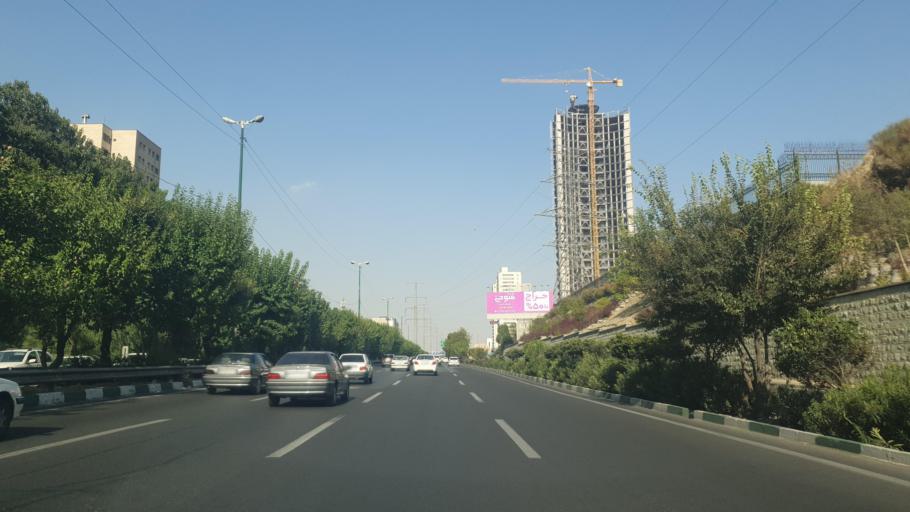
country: IR
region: Tehran
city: Tehran
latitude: 35.7506
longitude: 51.3909
